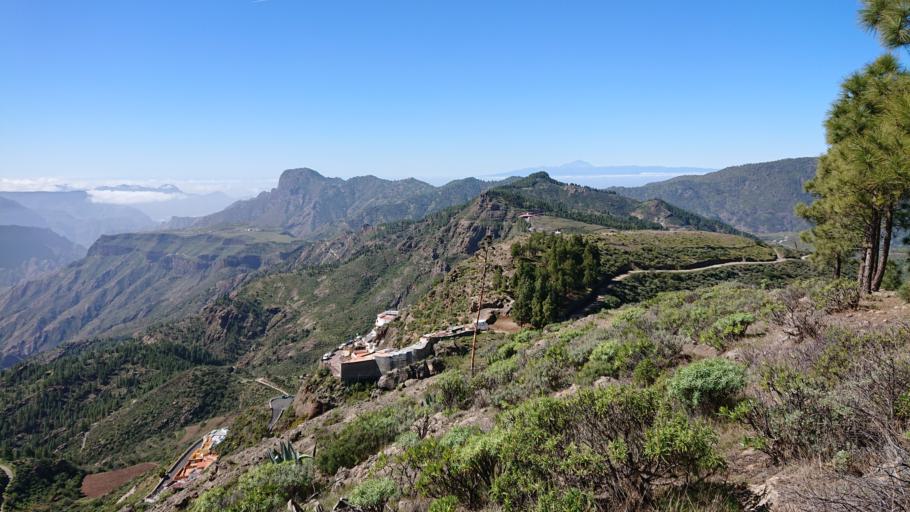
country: ES
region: Canary Islands
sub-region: Provincia de Las Palmas
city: Artenara
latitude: 28.0190
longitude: -15.6410
